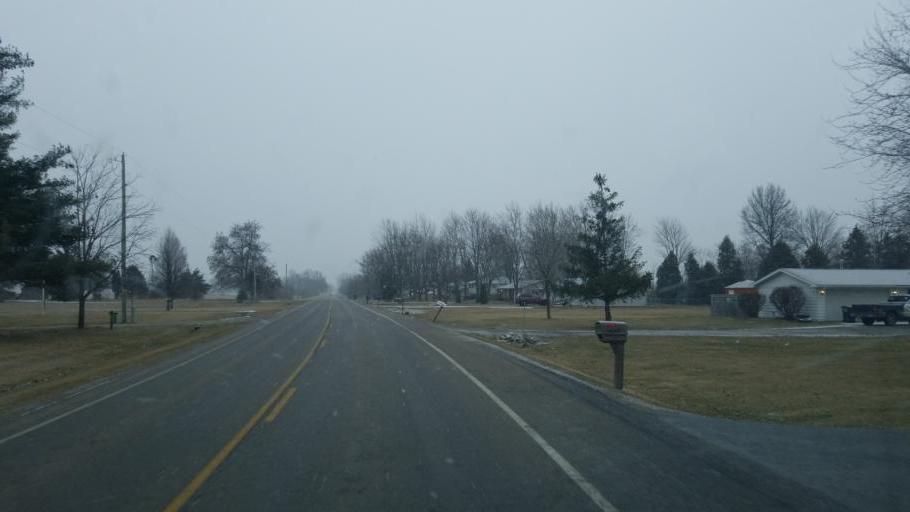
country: US
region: Ohio
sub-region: Defiance County
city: Hicksville
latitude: 41.3090
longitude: -84.7845
